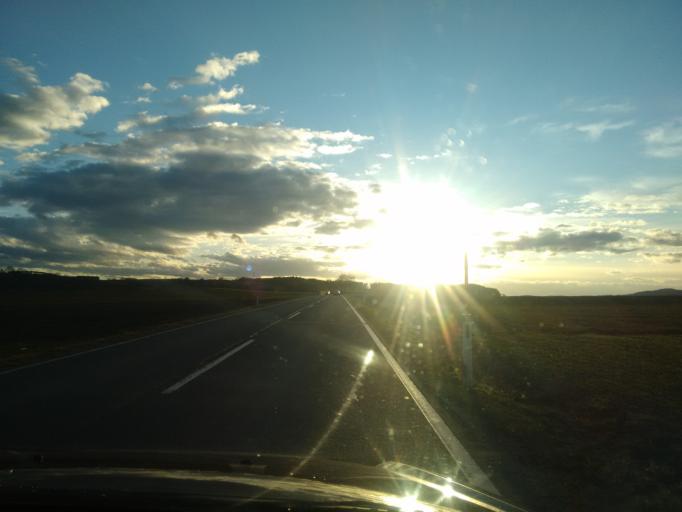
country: AT
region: Lower Austria
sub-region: Politischer Bezirk Melk
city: Petzenkirchen
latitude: 48.1655
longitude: 15.1514
